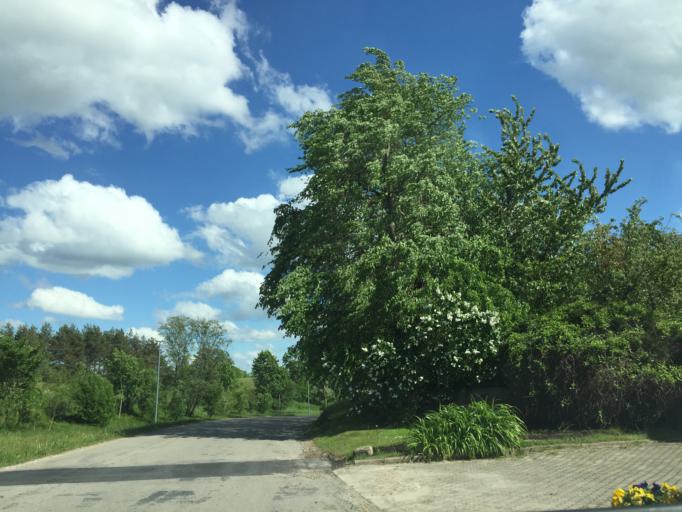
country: LV
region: Kandava
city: Kandava
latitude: 57.0434
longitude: 22.7798
